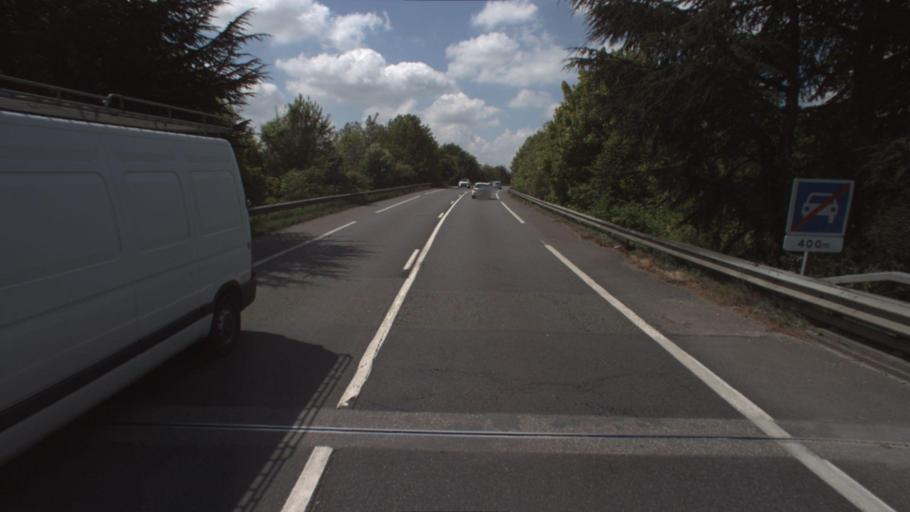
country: FR
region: Ile-de-France
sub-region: Departement de Seine-et-Marne
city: Guignes
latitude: 48.6386
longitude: 2.7922
